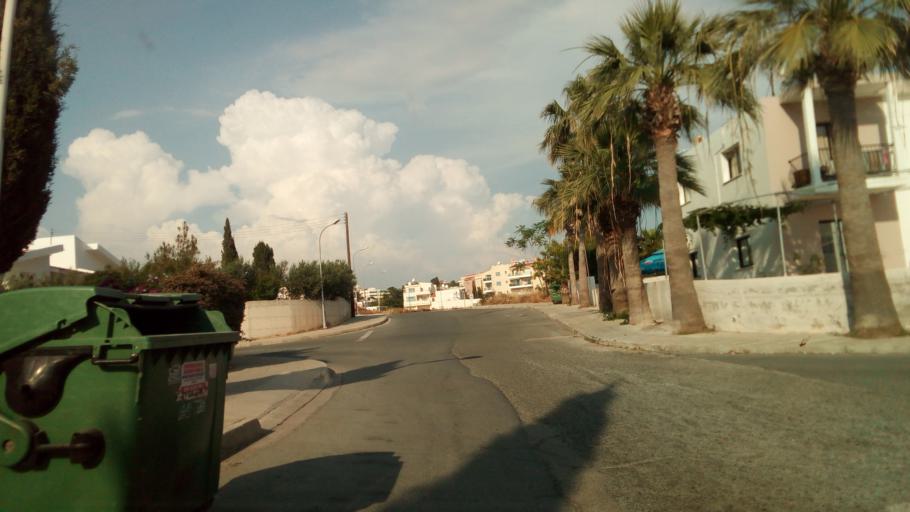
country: CY
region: Pafos
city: Paphos
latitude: 34.7719
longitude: 32.4135
